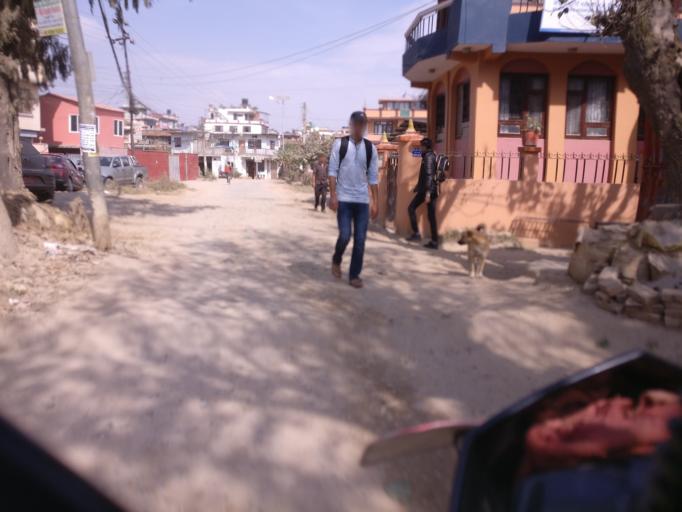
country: NP
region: Central Region
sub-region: Bagmati Zone
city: Patan
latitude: 27.6618
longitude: 85.3274
